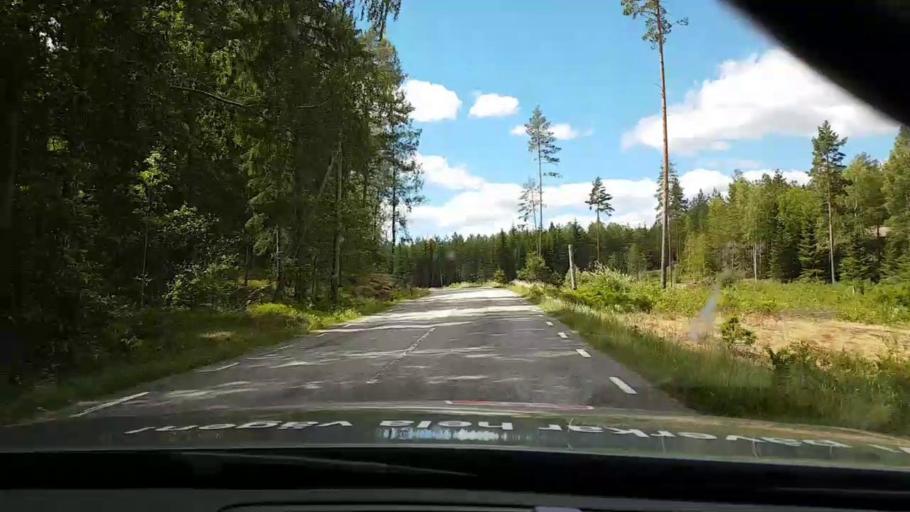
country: SE
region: Kalmar
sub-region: Vasterviks Kommun
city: Forserum
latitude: 58.0257
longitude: 16.5372
